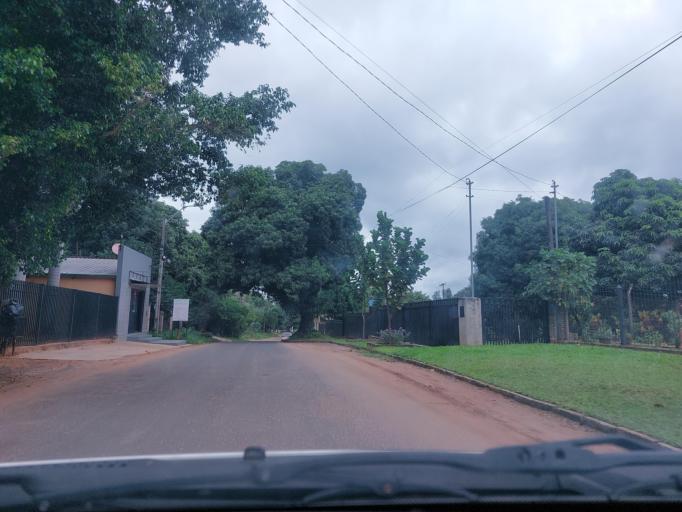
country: PY
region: San Pedro
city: Guayaybi
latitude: -24.6757
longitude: -56.4484
